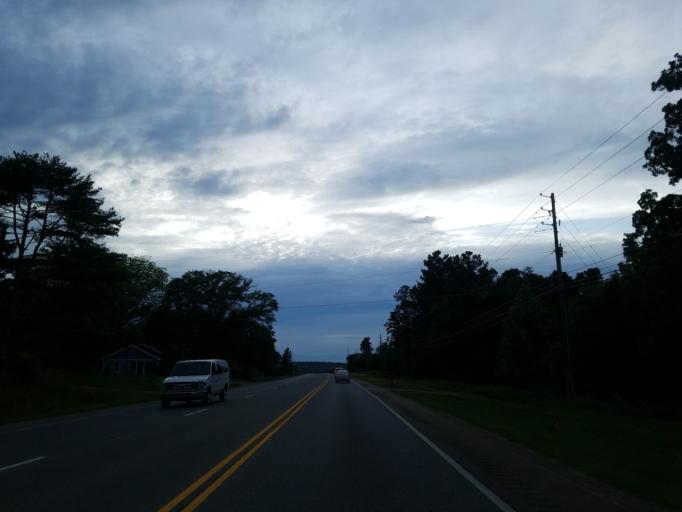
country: US
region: Georgia
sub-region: Cherokee County
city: Ball Ground
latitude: 34.2476
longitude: -84.3052
